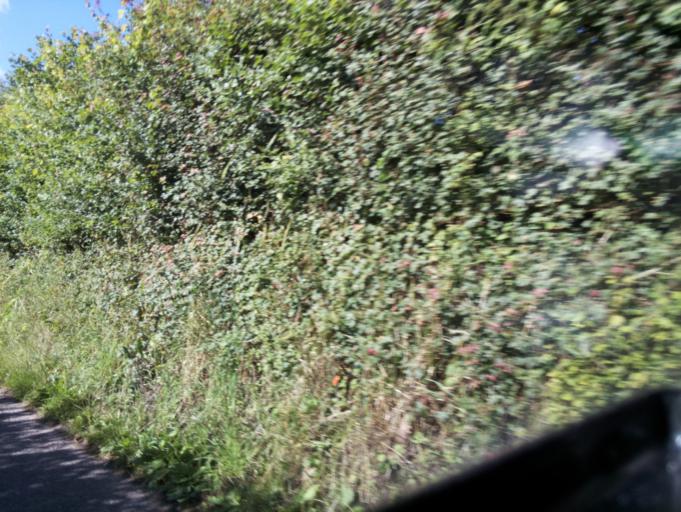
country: GB
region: England
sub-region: Herefordshire
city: Ross on Wye
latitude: 51.9444
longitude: -2.5733
